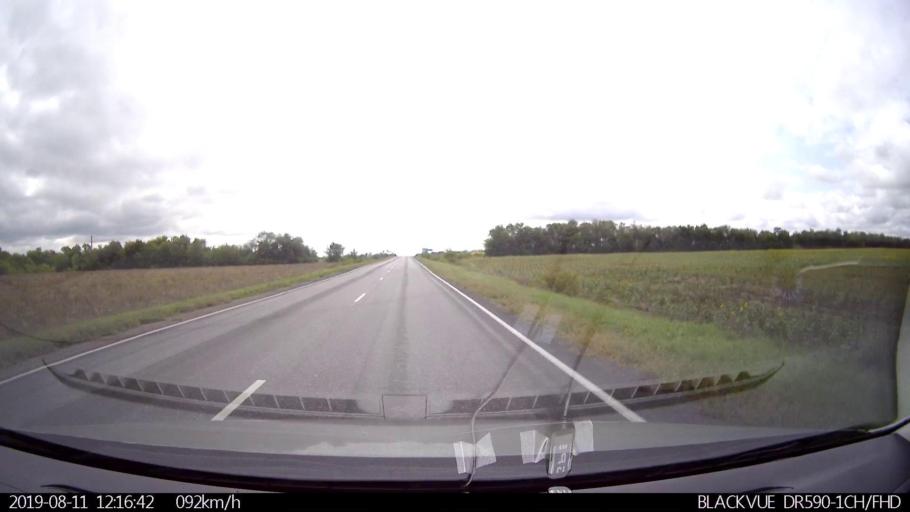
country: RU
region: Ulyanovsk
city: Ignatovka
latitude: 53.9260
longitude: 47.9594
